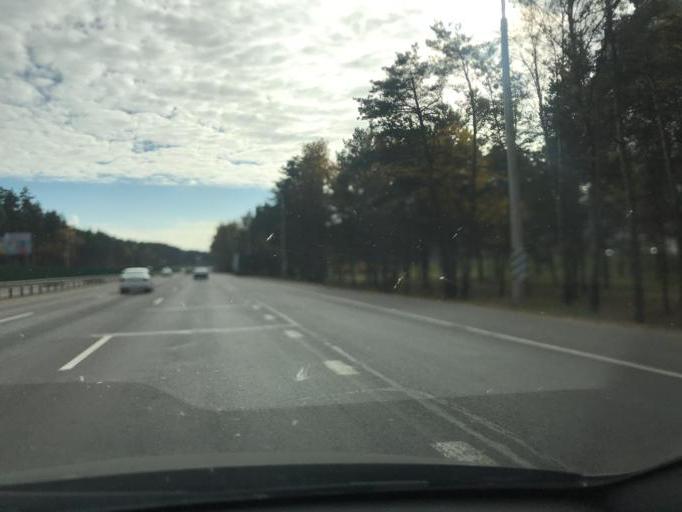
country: BY
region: Minsk
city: Vyaliki Trastsyanets
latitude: 53.8892
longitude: 27.6942
